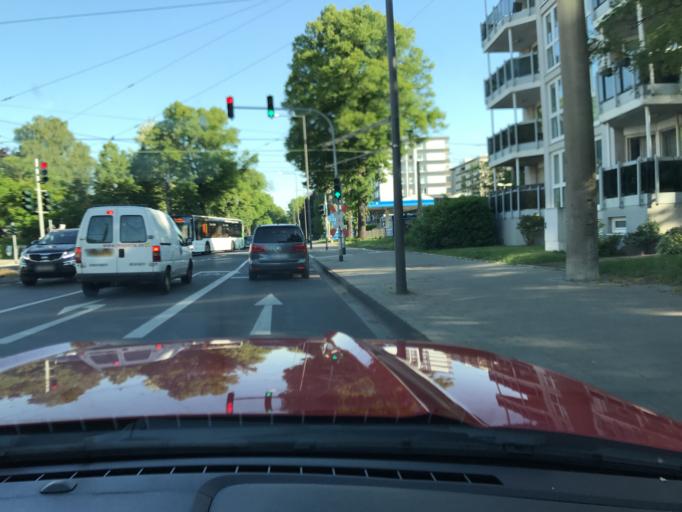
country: DE
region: North Rhine-Westphalia
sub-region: Regierungsbezirk Koln
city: Bilderstoeckchen
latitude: 50.9923
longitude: 6.9410
